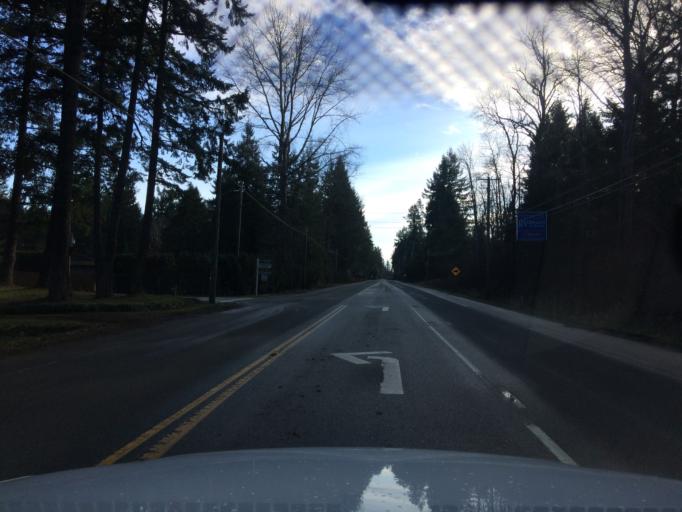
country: CA
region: British Columbia
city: Campbell River
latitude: 49.8887
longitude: -125.1351
